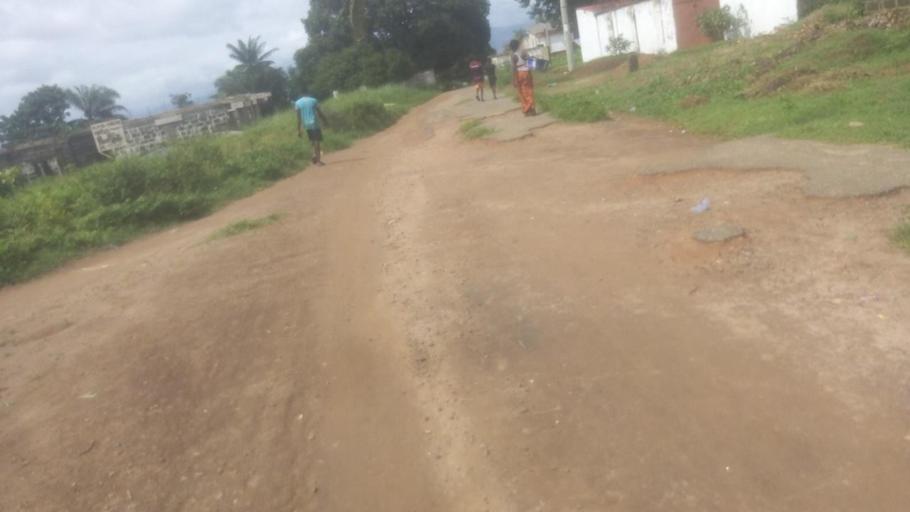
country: SL
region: Northern Province
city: Masoyila
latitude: 8.5871
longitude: -13.1996
